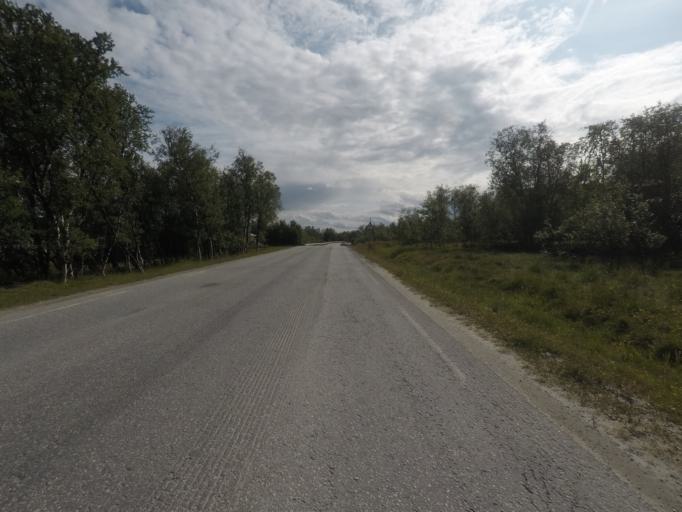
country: NO
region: Finnmark Fylke
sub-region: Porsanger
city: Lakselv
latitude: 70.1495
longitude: 24.9012
